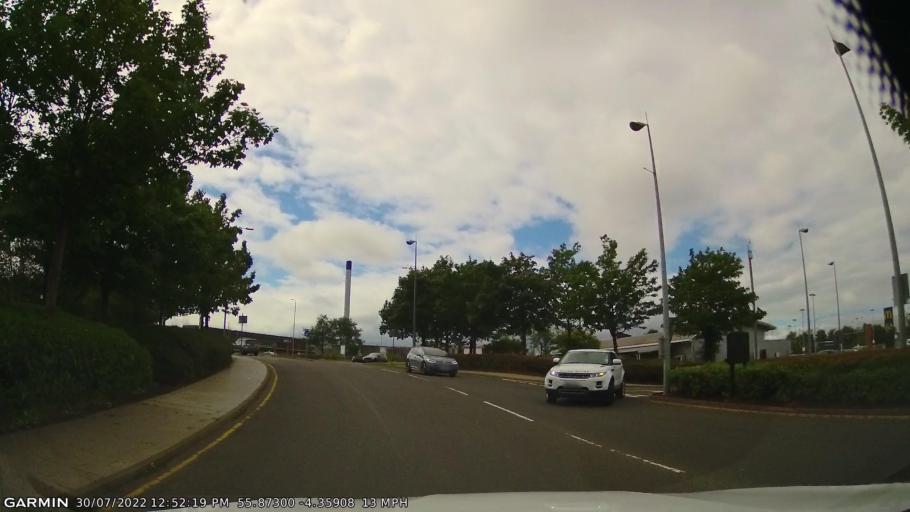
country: GB
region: Scotland
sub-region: Renfrewshire
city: Renfrew
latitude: 55.8733
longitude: -4.3591
